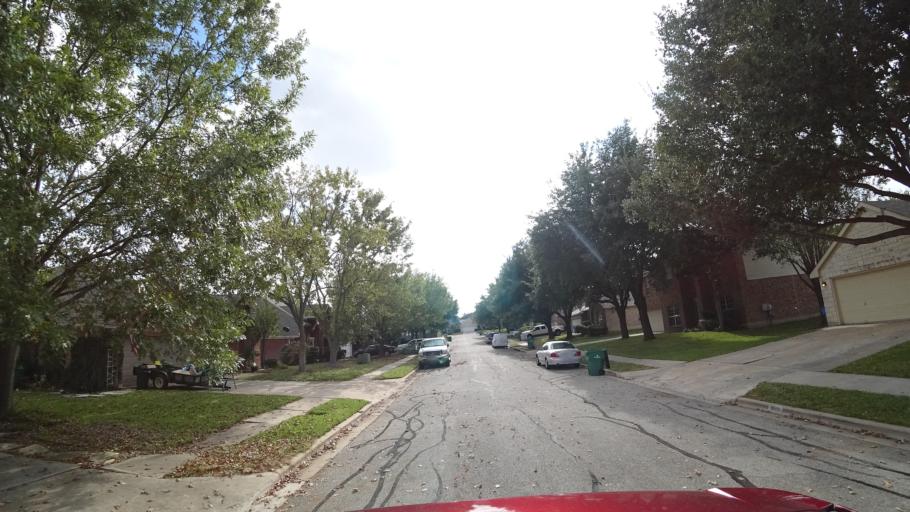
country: US
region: Texas
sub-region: Travis County
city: Pflugerville
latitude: 30.4326
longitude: -97.6265
